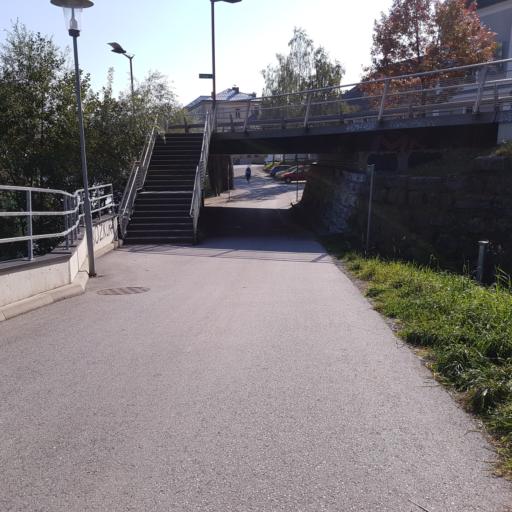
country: AT
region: Salzburg
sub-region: Politischer Bezirk Hallein
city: Hallein
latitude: 47.6849
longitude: 13.0897
